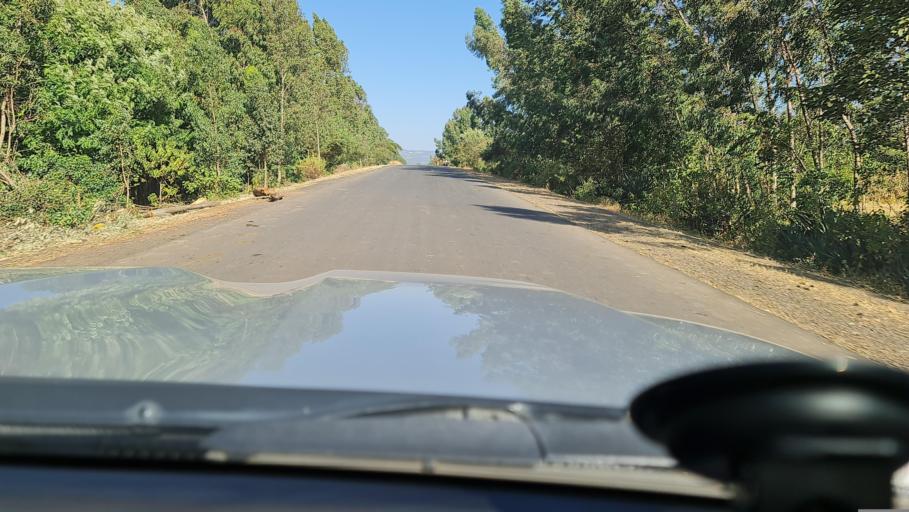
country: ET
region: Oromiya
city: Waliso
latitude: 8.5972
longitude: 37.9315
